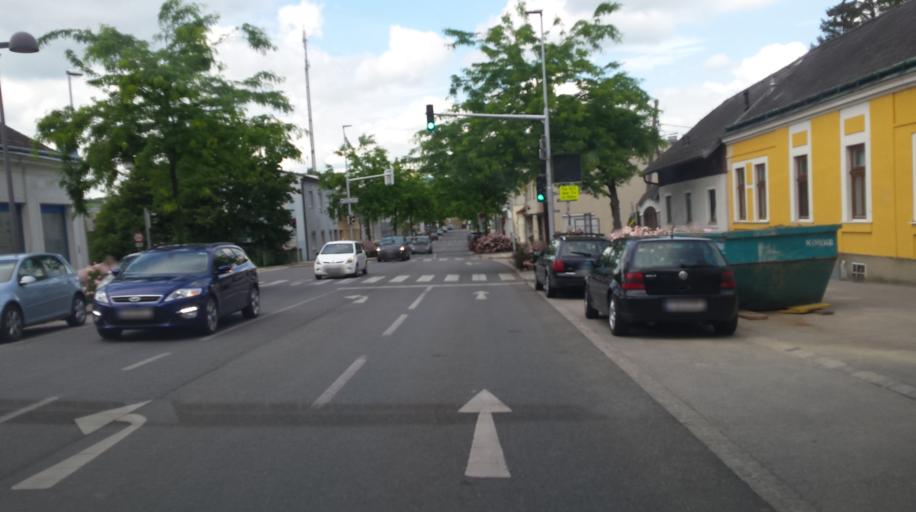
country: AT
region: Lower Austria
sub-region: Politischer Bezirk Mistelbach
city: Wolkersdorf im Weinviertel
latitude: 48.3825
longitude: 16.5134
